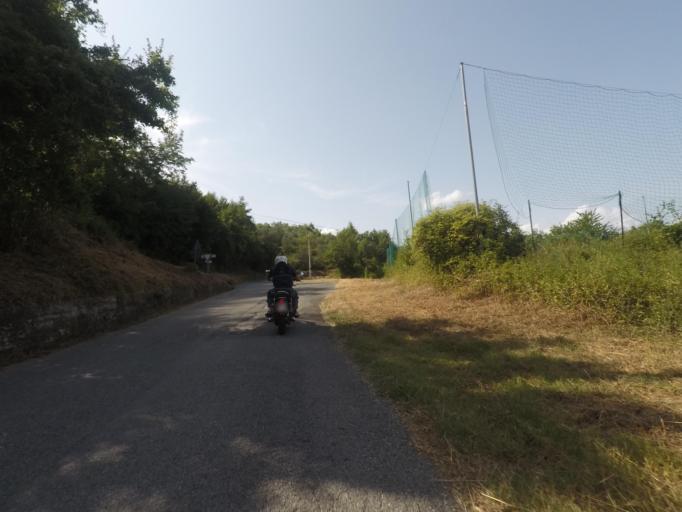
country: IT
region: Tuscany
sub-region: Provincia di Massa-Carrara
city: Fivizzano
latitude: 44.1690
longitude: 10.1025
